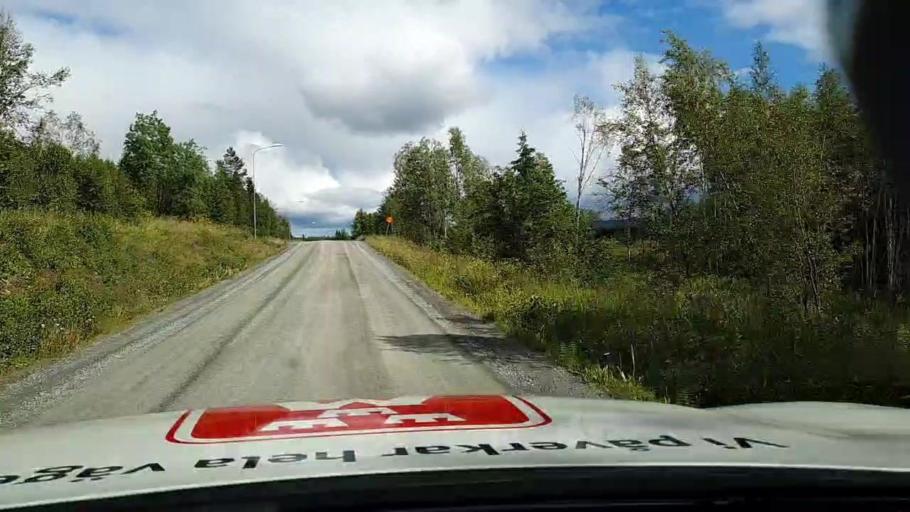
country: SE
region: Jaemtland
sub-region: Krokoms Kommun
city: Valla
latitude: 63.6939
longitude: 13.6574
